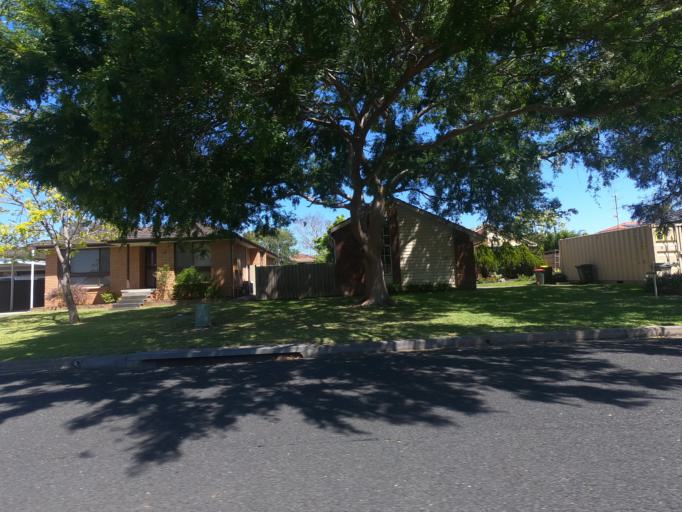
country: AU
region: New South Wales
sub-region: Wollongong
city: Dapto
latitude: -34.4899
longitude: 150.7822
